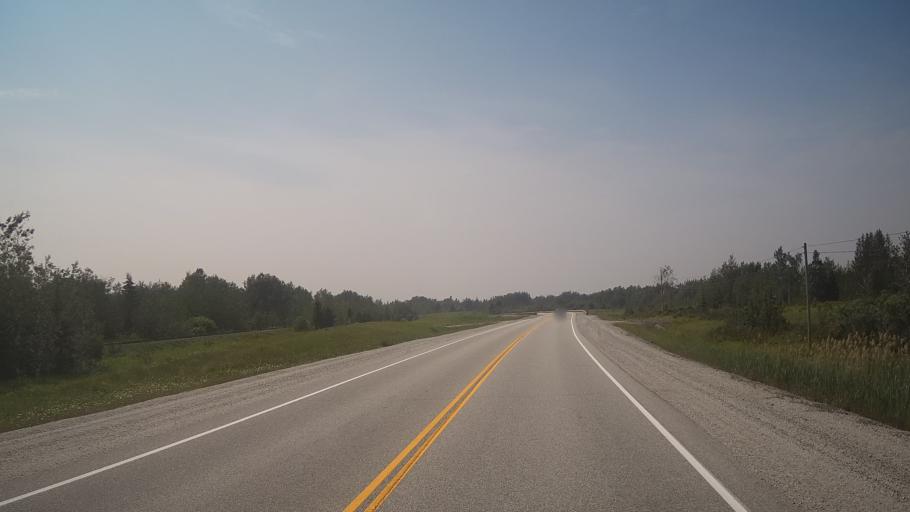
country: CA
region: Ontario
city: Kapuskasing
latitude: 49.2875
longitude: -81.7743
